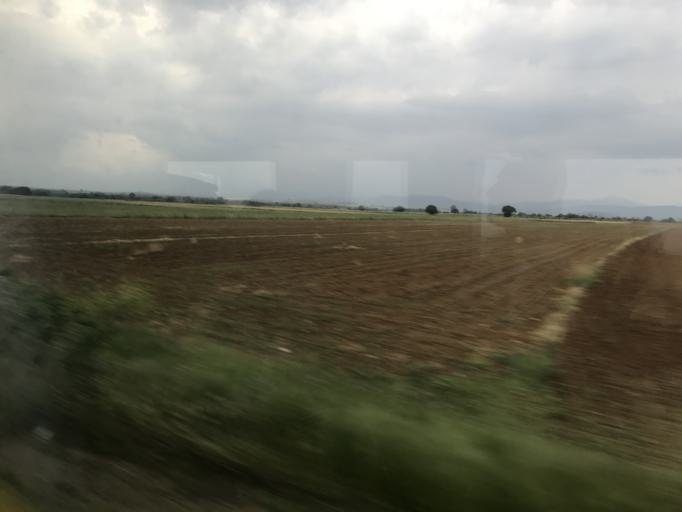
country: GR
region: East Macedonia and Thrace
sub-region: Nomos Rodopis
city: Aratos
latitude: 41.0852
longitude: 25.5262
